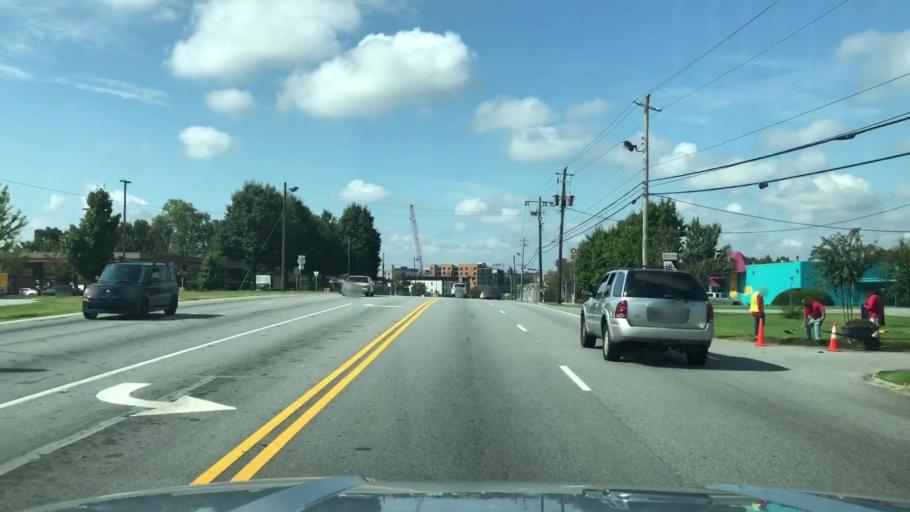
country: US
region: Georgia
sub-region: DeKalb County
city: Chamblee
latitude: 33.8955
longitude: -84.3049
